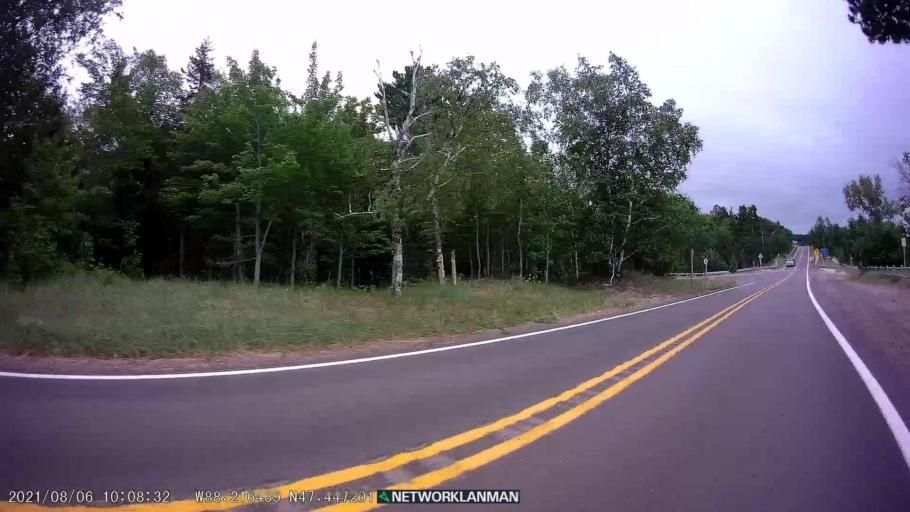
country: US
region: Michigan
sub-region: Keweenaw County
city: Eagle River
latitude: 47.4467
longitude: -88.2165
